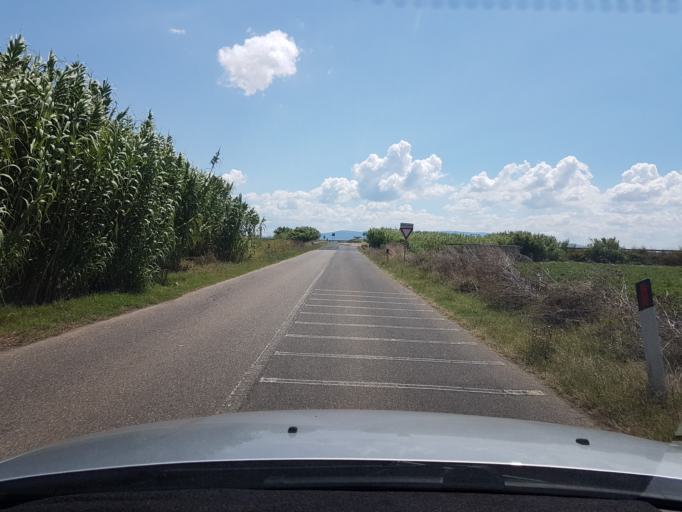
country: IT
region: Sardinia
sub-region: Provincia di Oristano
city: Solanas
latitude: 39.9186
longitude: 8.5523
